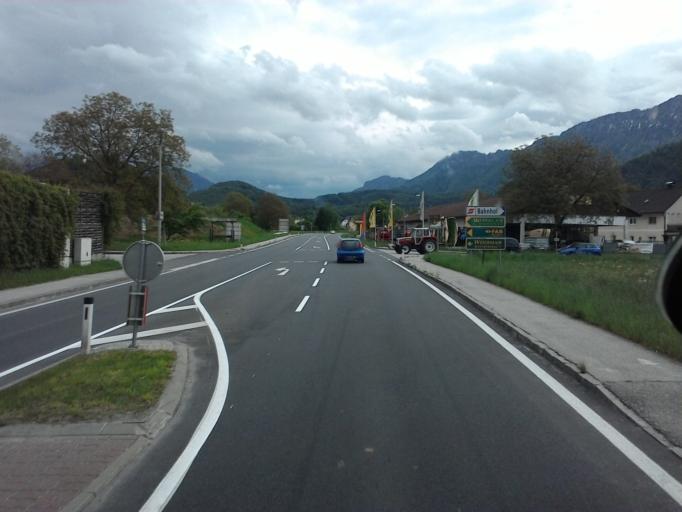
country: AT
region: Upper Austria
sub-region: Politischer Bezirk Kirchdorf an der Krems
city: Micheldorf in Oberoesterreich
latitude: 47.8833
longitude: 14.1277
